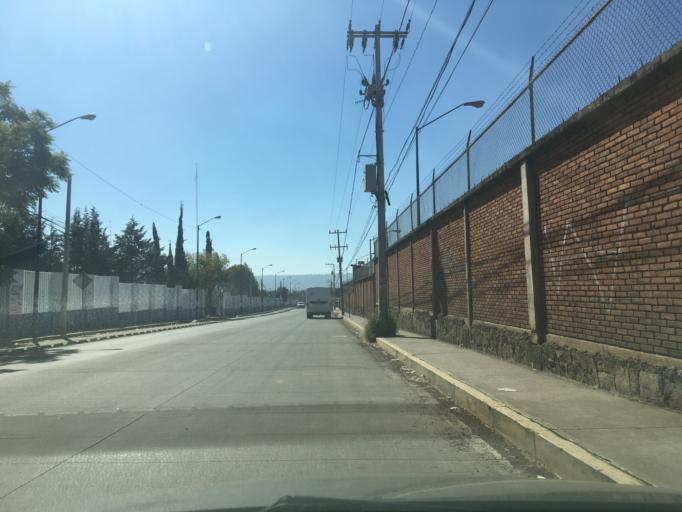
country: MX
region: Michoacan
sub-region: Morelia
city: San Antonio
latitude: 19.6912
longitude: -101.2505
